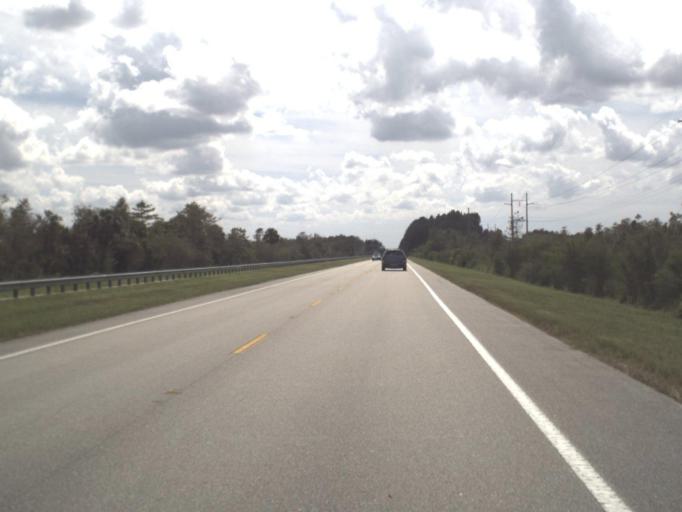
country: US
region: Florida
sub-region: Collier County
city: Lely Resort
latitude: 26.0095
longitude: -81.3463
